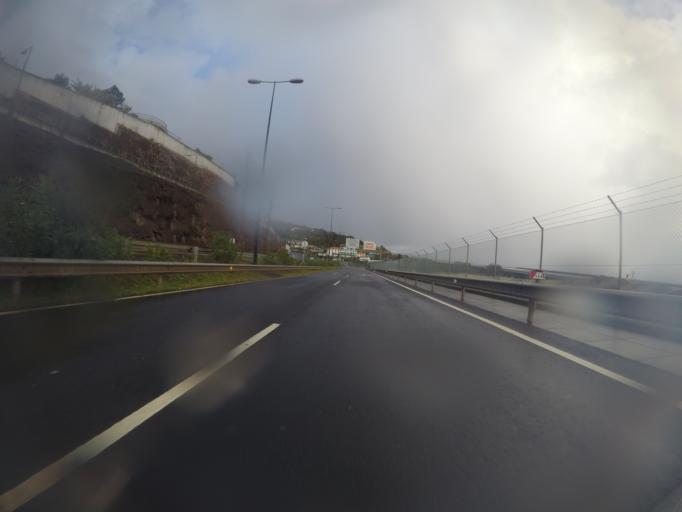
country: PT
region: Madeira
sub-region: Machico
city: Machico
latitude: 32.7050
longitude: -16.7684
